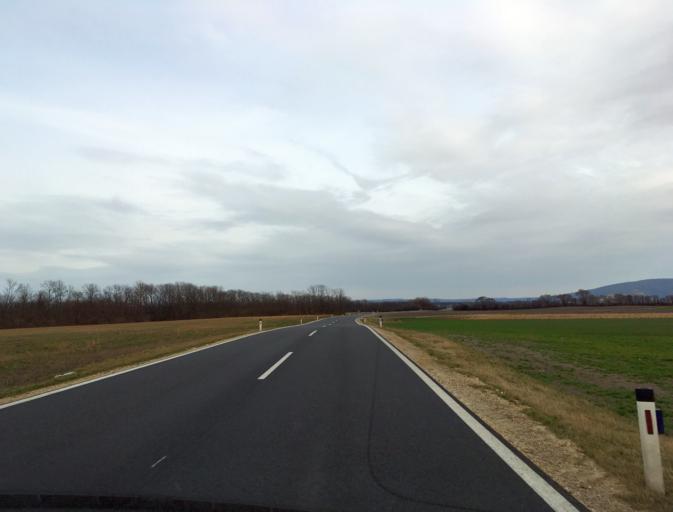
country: AT
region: Lower Austria
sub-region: Politischer Bezirk Ganserndorf
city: Lassee
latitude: 48.2225
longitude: 16.8683
